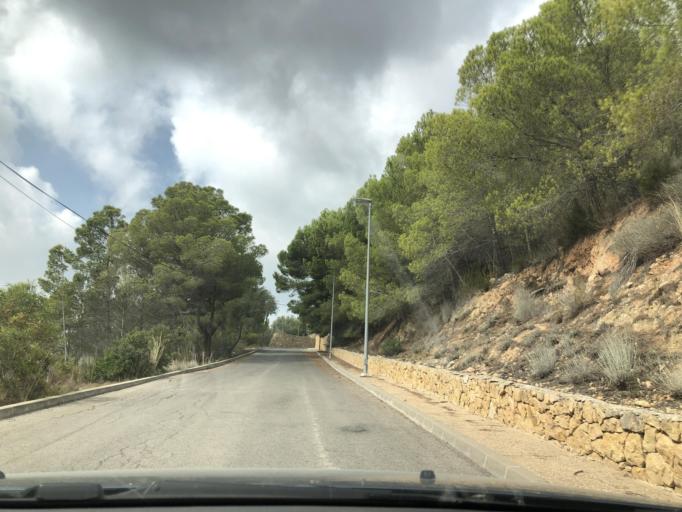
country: ES
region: Valencia
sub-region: Provincia de Alicante
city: Altea
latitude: 38.6401
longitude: -0.0677
